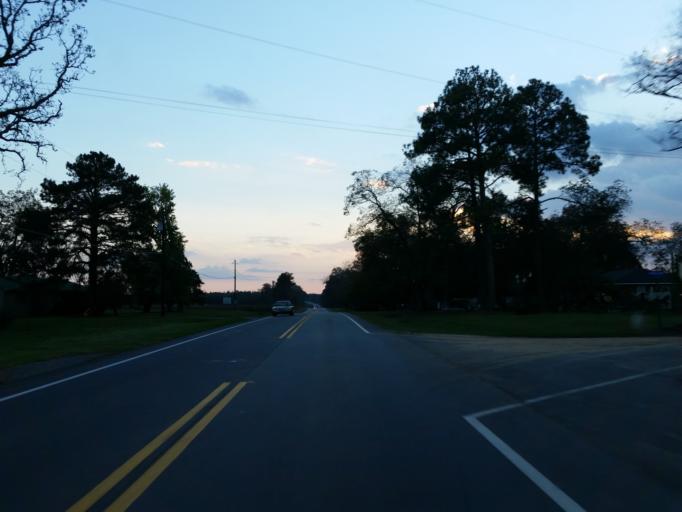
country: US
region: Georgia
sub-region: Pulaski County
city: Hawkinsville
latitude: 32.2644
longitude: -83.4858
